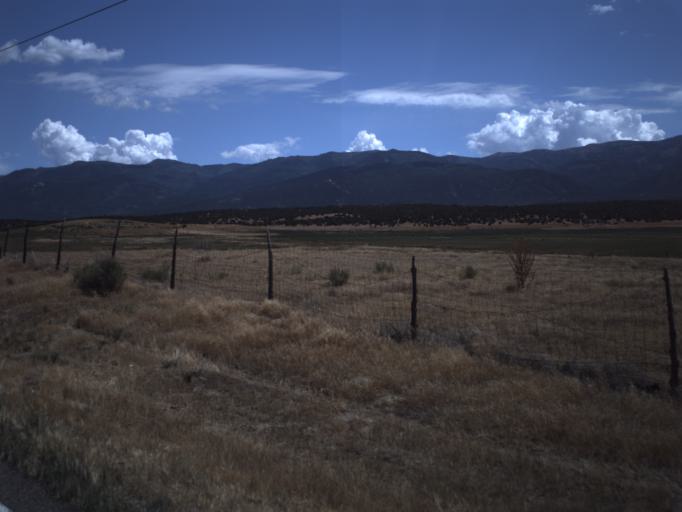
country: US
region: Utah
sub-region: Sanpete County
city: Moroni
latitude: 39.4798
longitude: -111.5365
